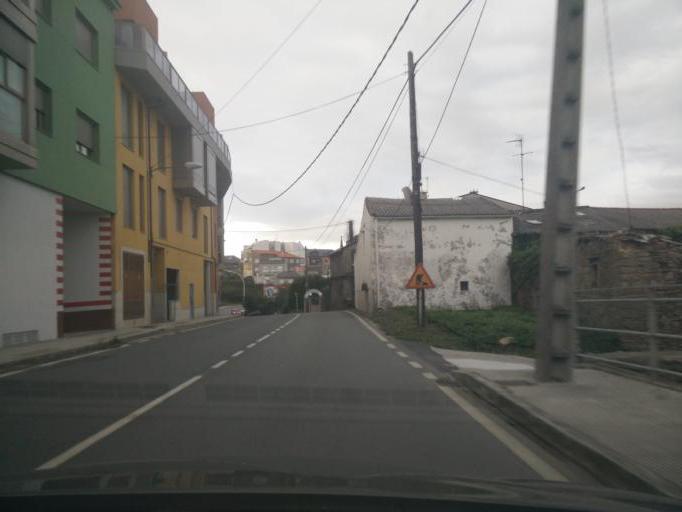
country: ES
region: Galicia
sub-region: Provincia da Coruna
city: A Coruna
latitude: 43.3391
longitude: -8.4205
